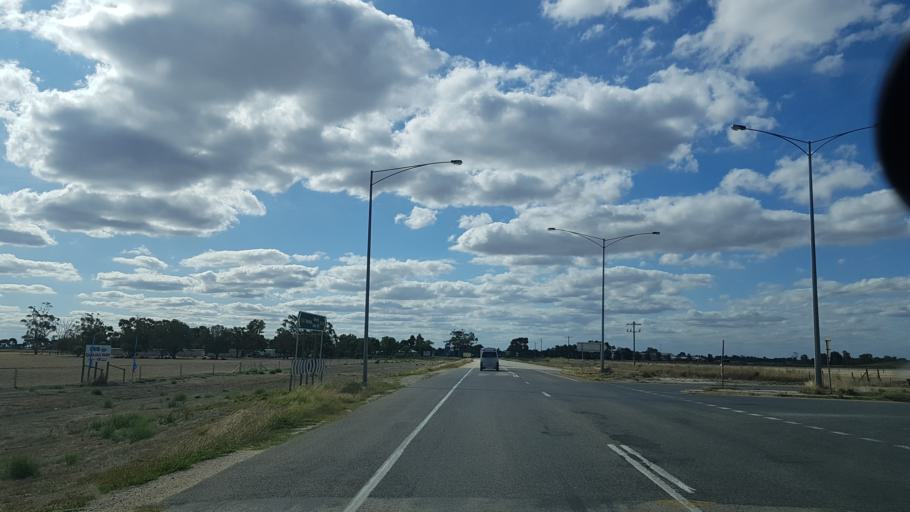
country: AU
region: Victoria
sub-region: Swan Hill
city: Swan Hill
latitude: -35.7634
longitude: 143.9313
